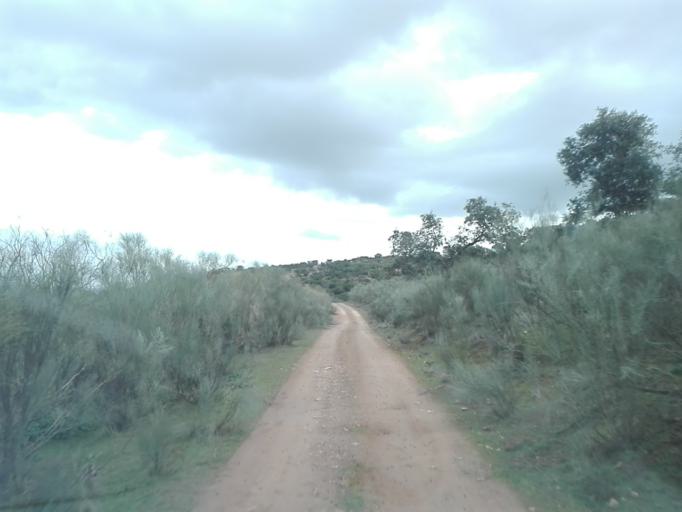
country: ES
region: Extremadura
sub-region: Provincia de Badajoz
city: Hinojosa del Valle
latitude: 38.4421
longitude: -6.1875
